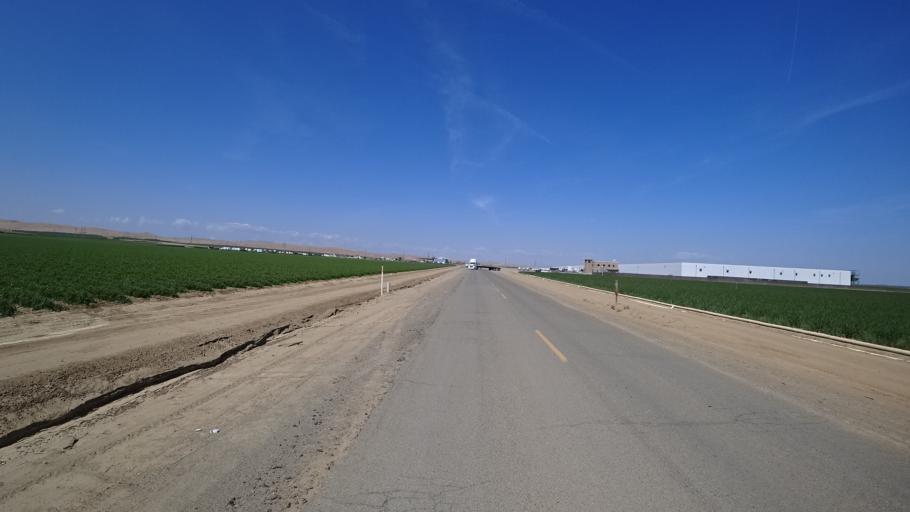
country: US
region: California
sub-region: Kings County
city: Kettleman City
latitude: 36.0725
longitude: -120.0437
